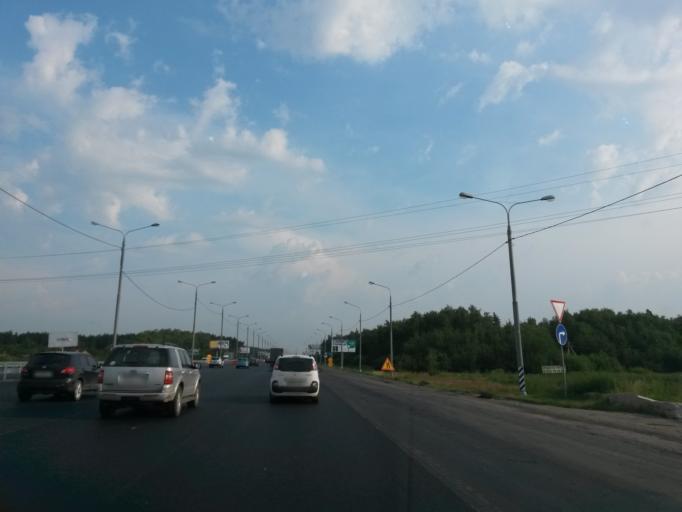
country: RU
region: Moskovskaya
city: Shcherbinka
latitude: 55.4857
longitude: 37.6135
